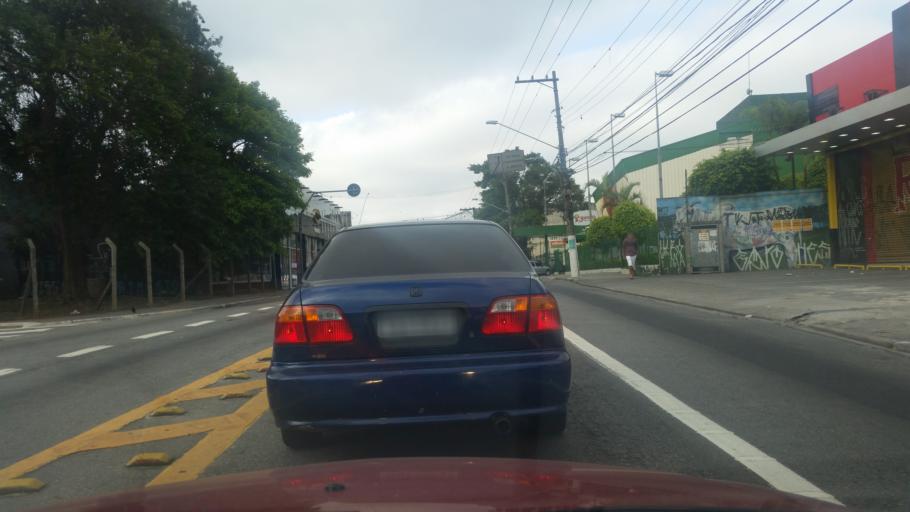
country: BR
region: Sao Paulo
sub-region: Diadema
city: Diadema
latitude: -23.7148
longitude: -46.6990
